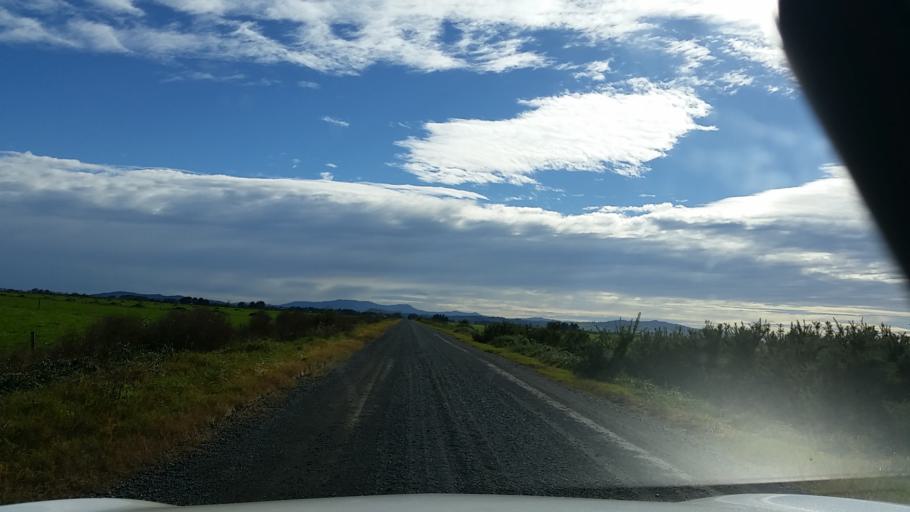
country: NZ
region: Waikato
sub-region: Hamilton City
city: Hamilton
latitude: -37.6877
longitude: 175.4456
